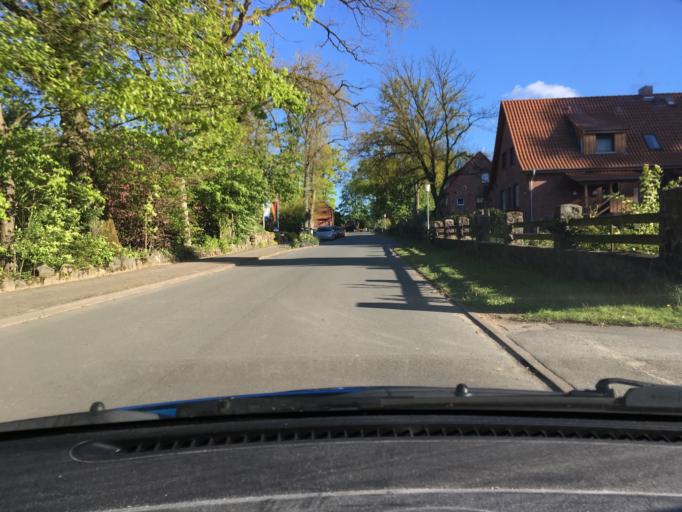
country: DE
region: Lower Saxony
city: Soderstorf
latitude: 53.1285
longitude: 10.1679
